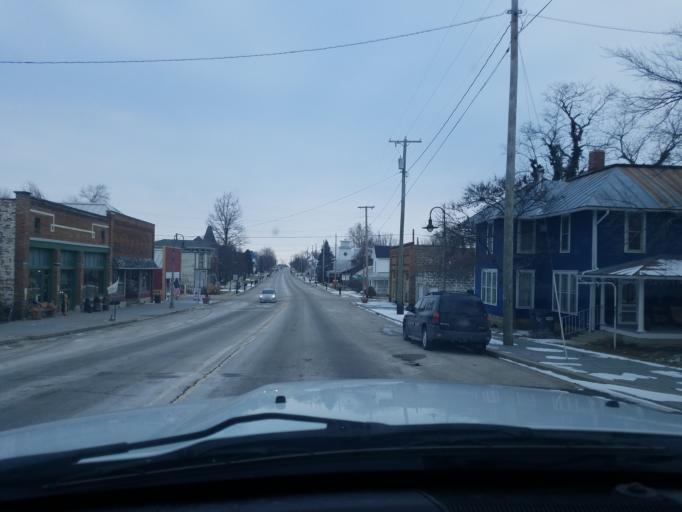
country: US
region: Indiana
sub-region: Randolph County
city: Farmland
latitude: 40.1886
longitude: -85.1277
